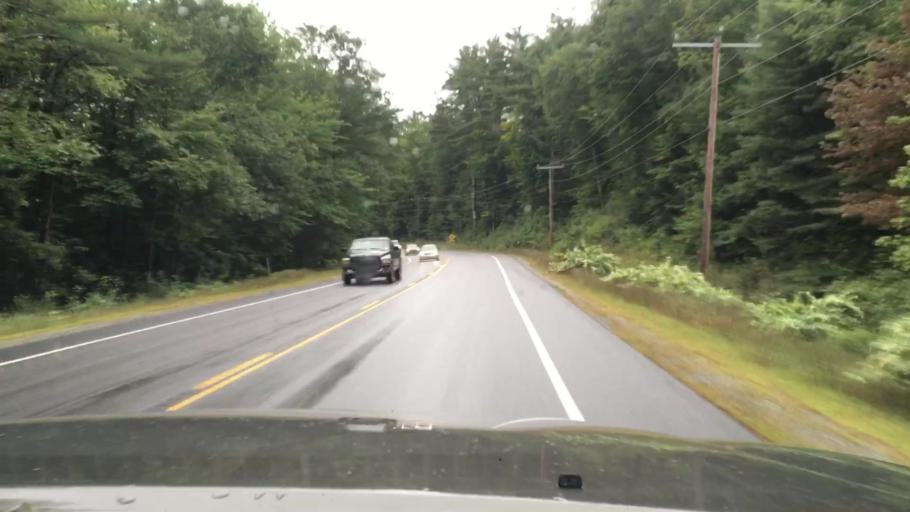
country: US
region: New Hampshire
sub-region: Hillsborough County
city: Antrim
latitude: 43.0917
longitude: -71.9669
